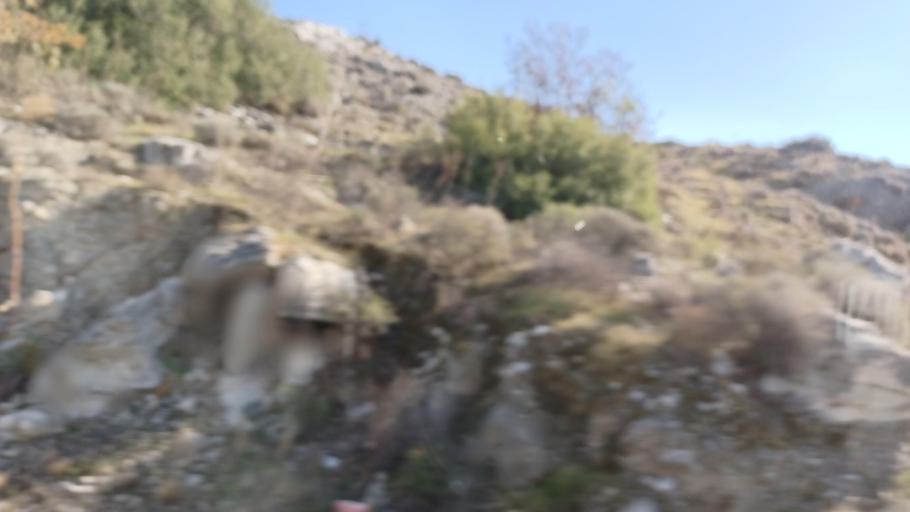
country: CY
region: Larnaka
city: Kofinou
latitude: 34.7664
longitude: 33.3259
